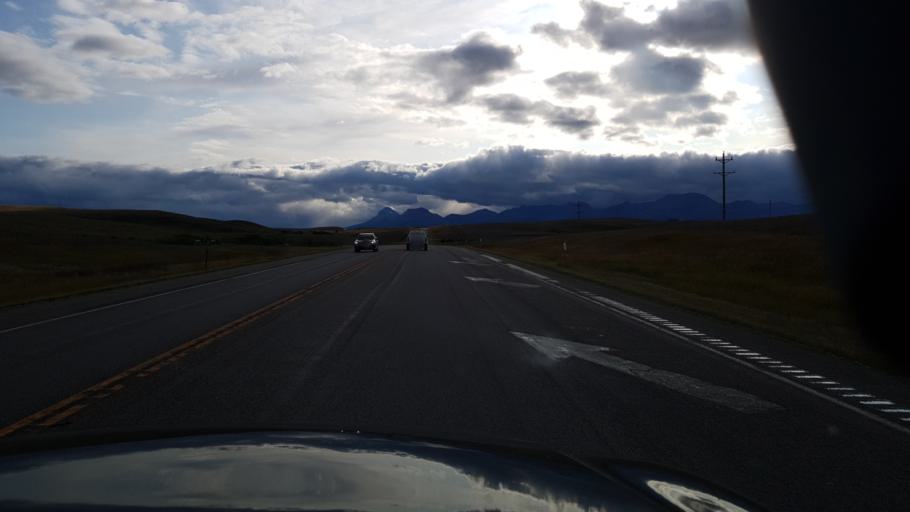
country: US
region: Montana
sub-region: Glacier County
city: South Browning
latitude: 48.5069
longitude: -113.1019
